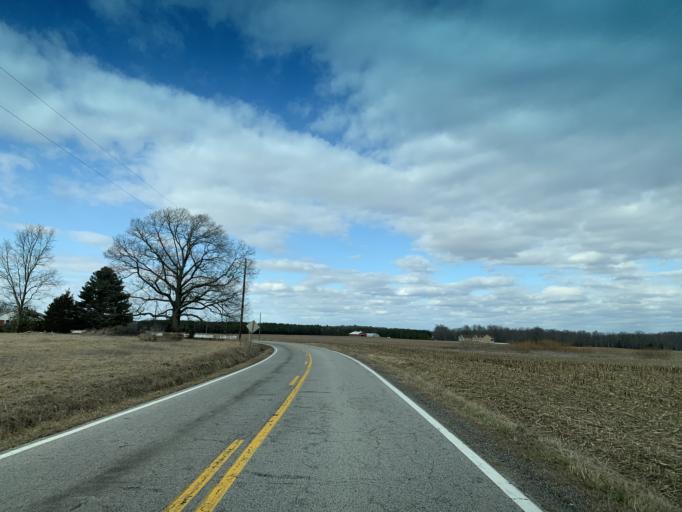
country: US
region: Maryland
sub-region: Caroline County
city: Ridgely
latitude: 38.9483
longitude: -75.9795
